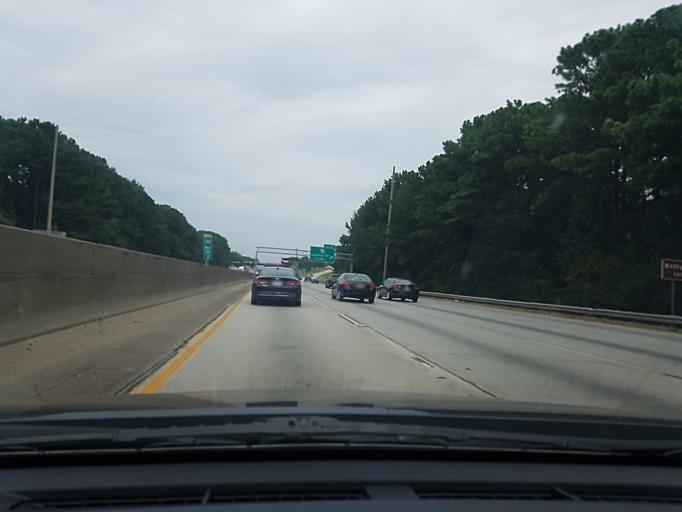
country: US
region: Georgia
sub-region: DeKalb County
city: Clarkston
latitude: 33.8402
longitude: -84.2480
